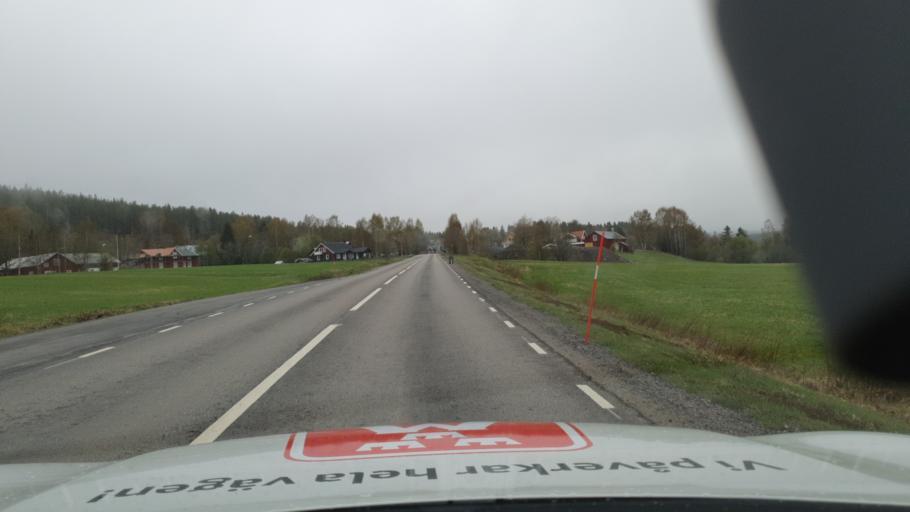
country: SE
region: Vaesterbotten
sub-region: Vannas Kommun
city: Vannasby
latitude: 63.7793
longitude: 19.8459
